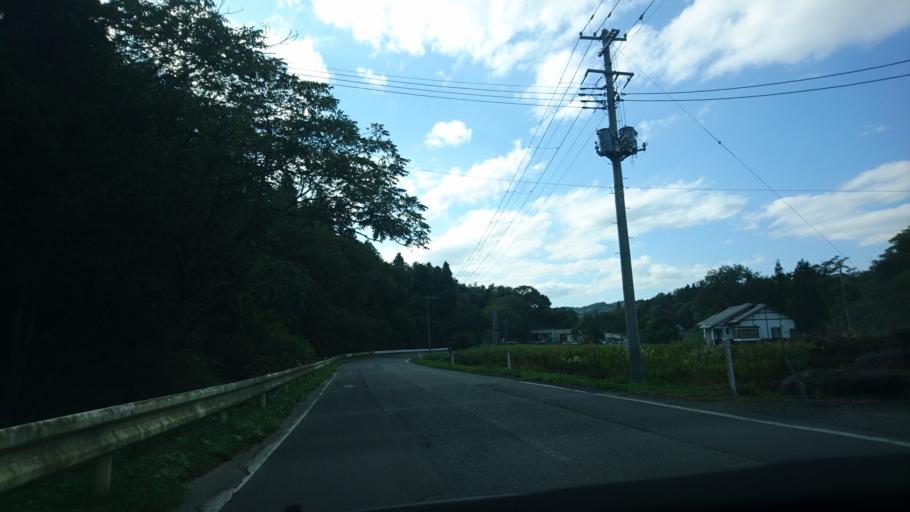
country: JP
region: Iwate
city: Ichinoseki
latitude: 38.8704
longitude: 141.3506
